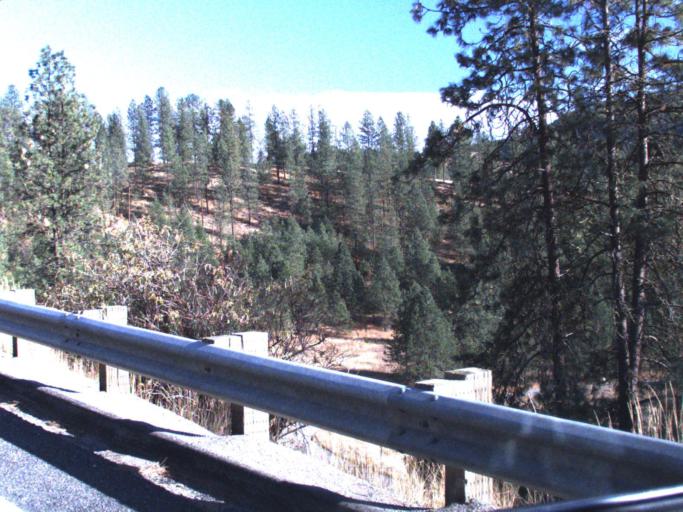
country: US
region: Washington
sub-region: Stevens County
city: Kettle Falls
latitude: 48.5798
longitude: -118.0773
